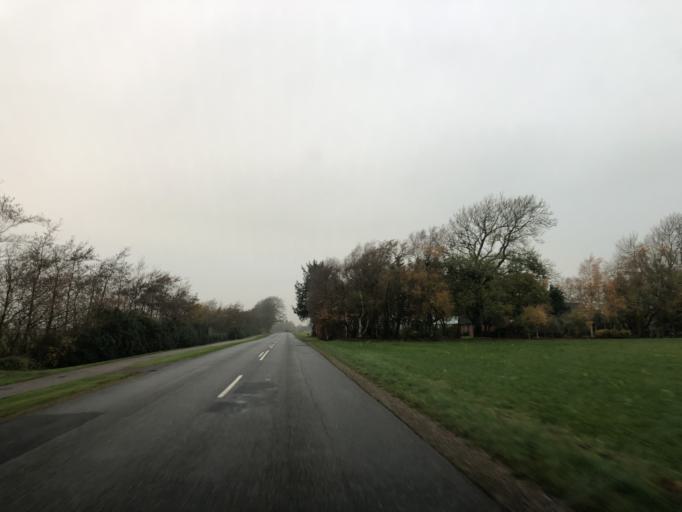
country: DK
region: Central Jutland
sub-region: Herning Kommune
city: Vildbjerg
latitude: 56.2125
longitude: 8.7510
